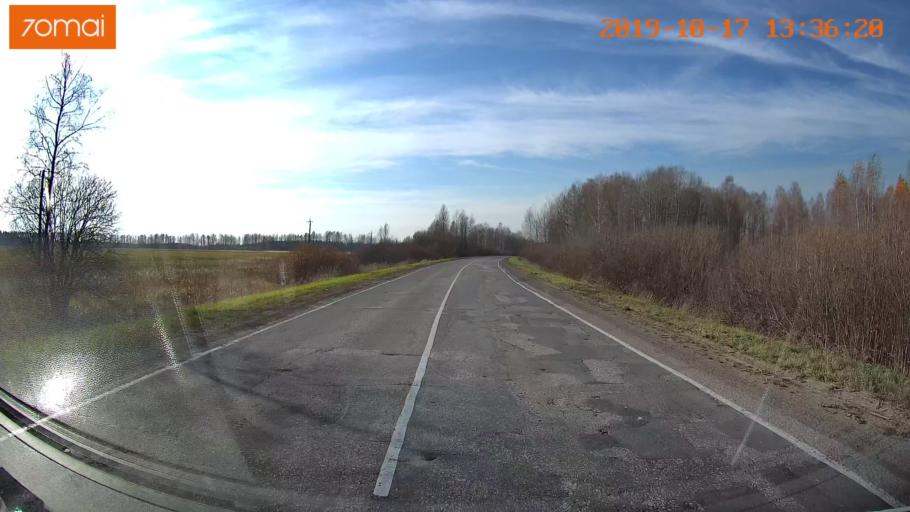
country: RU
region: Vladimir
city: Velikodvorskiy
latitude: 55.1397
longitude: 40.6668
